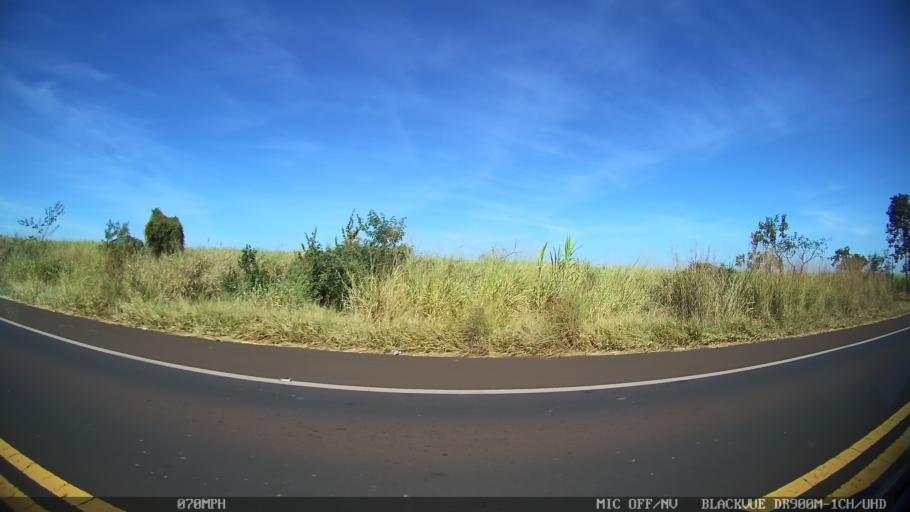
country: BR
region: Sao Paulo
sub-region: Franca
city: Franca
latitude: -20.5580
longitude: -47.5971
